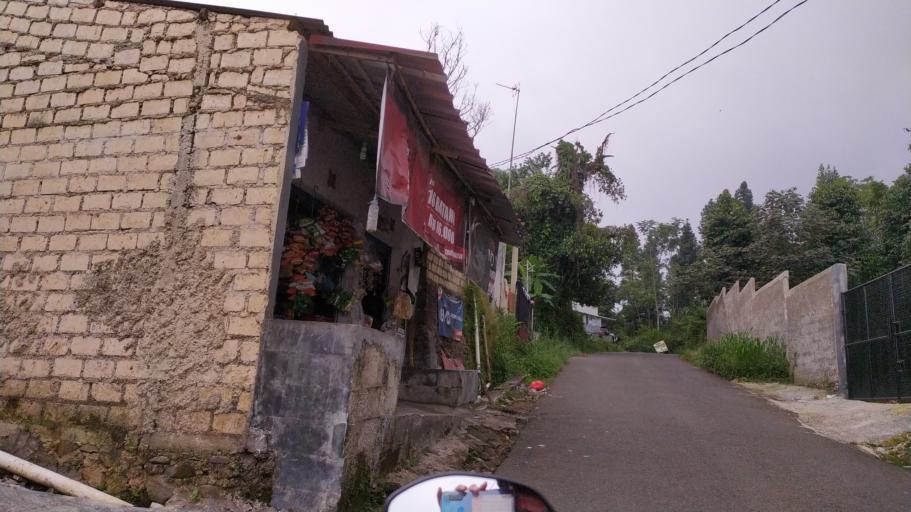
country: ID
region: West Java
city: Bogor
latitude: -6.6553
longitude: 106.7107
